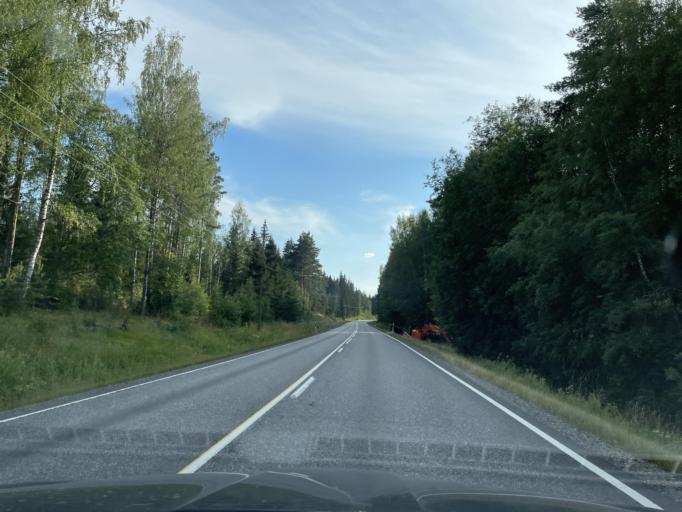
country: FI
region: Paijanne Tavastia
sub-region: Lahti
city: Padasjoki
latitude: 61.3344
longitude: 25.2192
